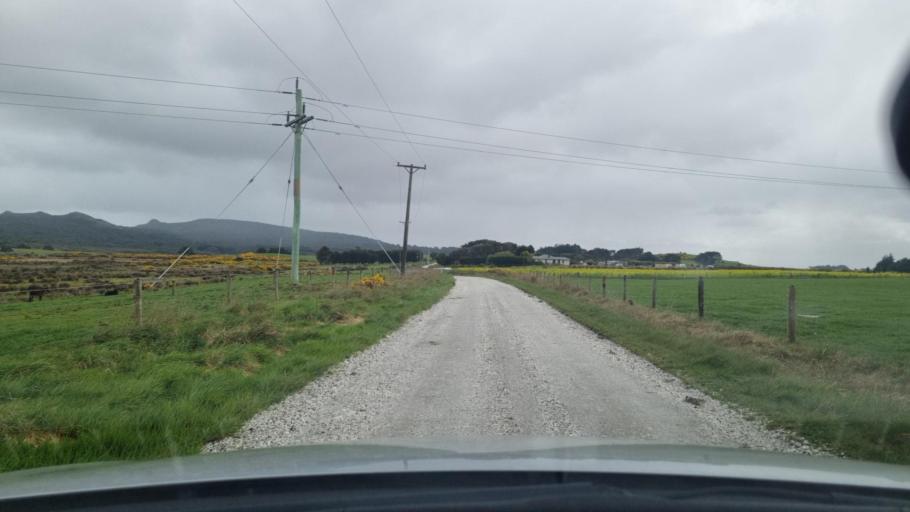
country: NZ
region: Southland
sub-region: Invercargill City
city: Bluff
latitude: -46.5448
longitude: 168.2977
